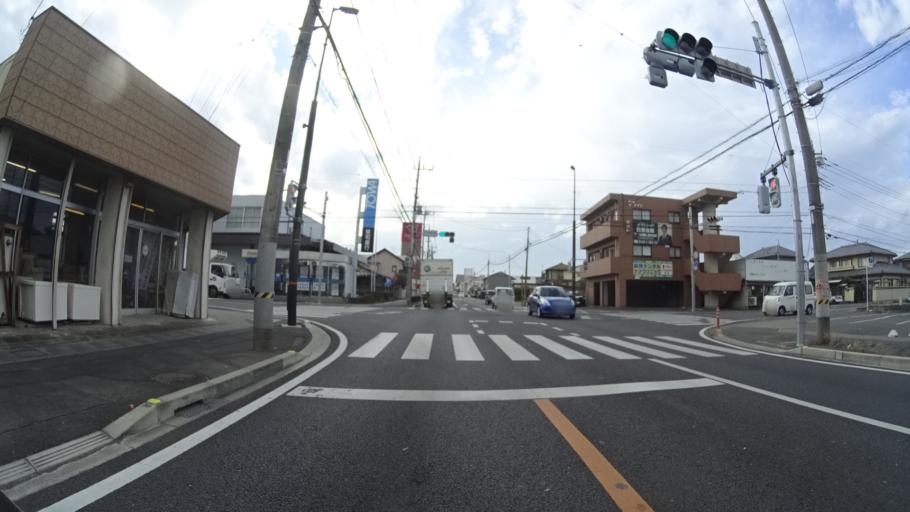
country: JP
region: Gunma
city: Maebashi-shi
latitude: 36.3945
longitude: 139.0889
